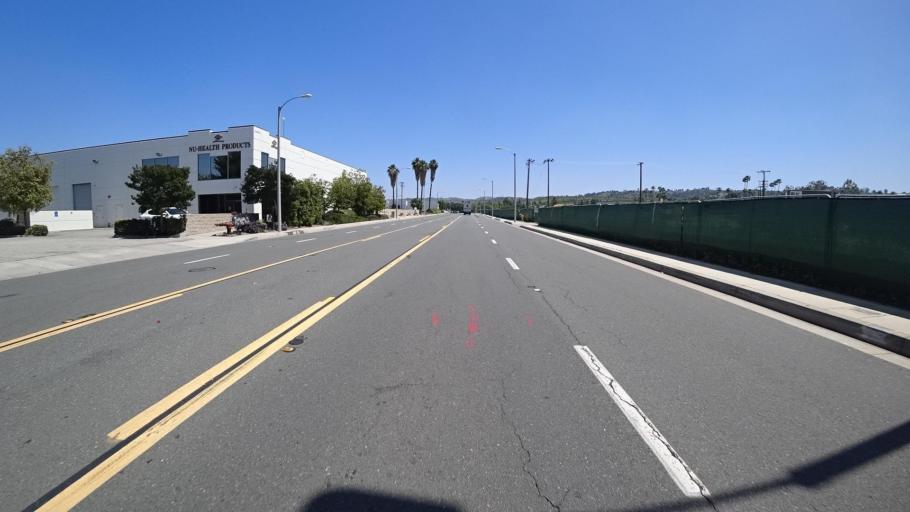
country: US
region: California
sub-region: Los Angeles County
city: Walnut
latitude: 34.0082
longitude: -117.8500
